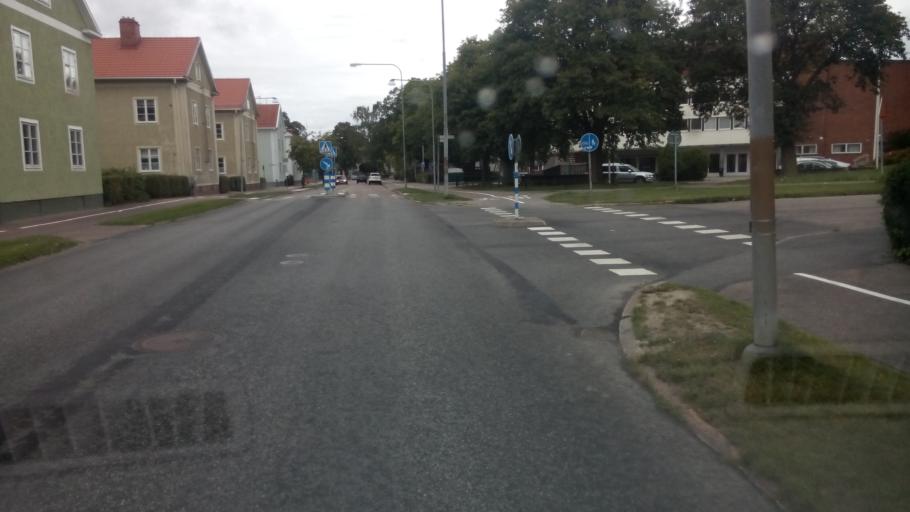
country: SE
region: Soedermanland
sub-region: Nykopings Kommun
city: Nykoping
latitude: 58.7547
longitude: 17.0224
